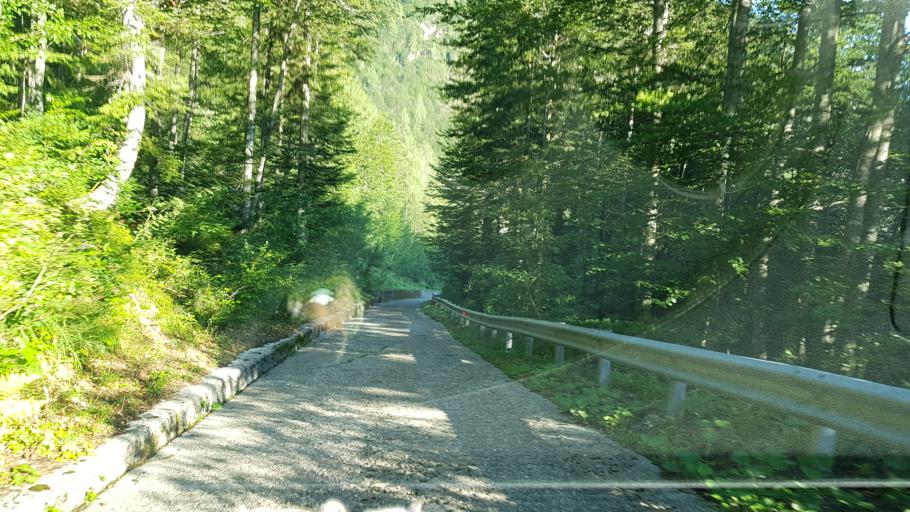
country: IT
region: Friuli Venezia Giulia
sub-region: Provincia di Udine
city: Pontebba
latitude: 46.4785
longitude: 13.2535
